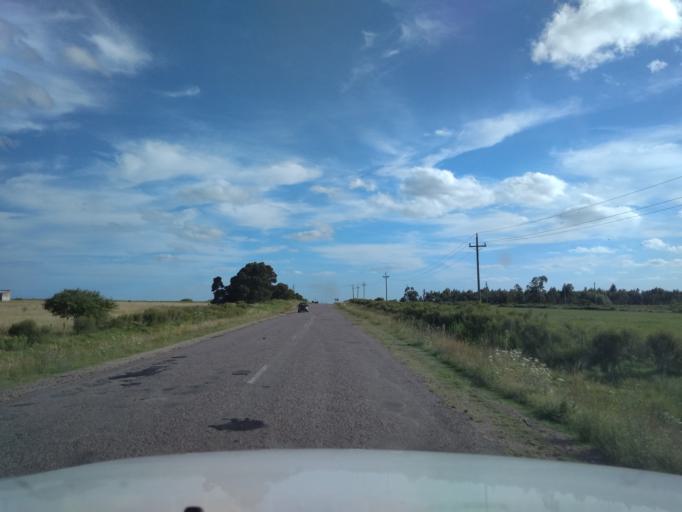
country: UY
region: Canelones
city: San Ramon
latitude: -34.2567
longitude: -55.9268
